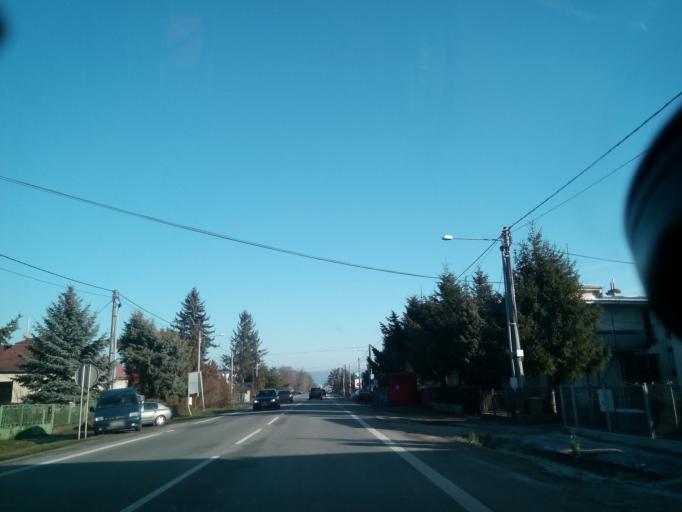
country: SK
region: Kosicky
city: Michalovce
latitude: 48.7340
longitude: 21.8853
